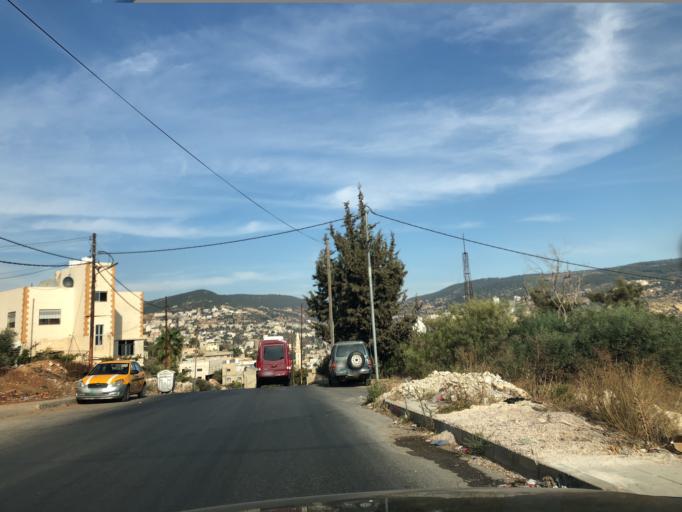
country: JO
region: Ajlun
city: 'Ajlun
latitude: 32.3304
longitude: 35.7403
